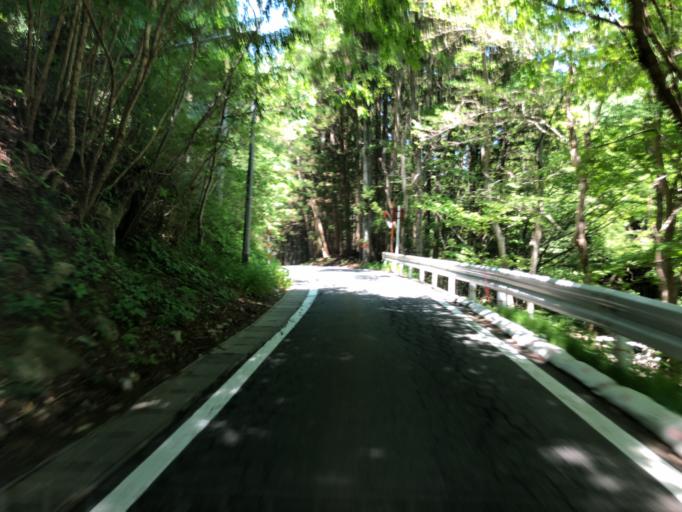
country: JP
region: Fukushima
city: Namie
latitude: 37.5235
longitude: 140.8524
